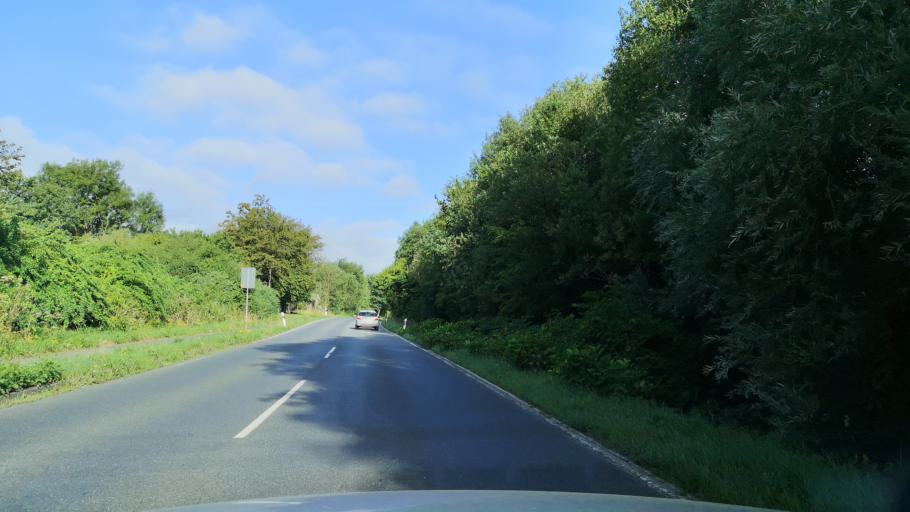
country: DE
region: North Rhine-Westphalia
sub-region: Regierungsbezirk Dusseldorf
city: Wuppertal
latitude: 51.3048
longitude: 7.1197
